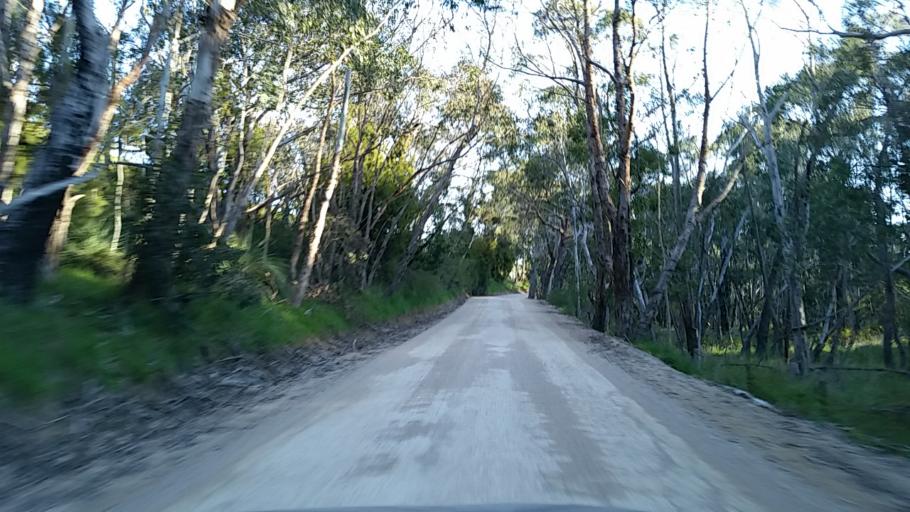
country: AU
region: South Australia
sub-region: Alexandrina
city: Mount Compass
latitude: -35.2750
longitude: 138.7014
